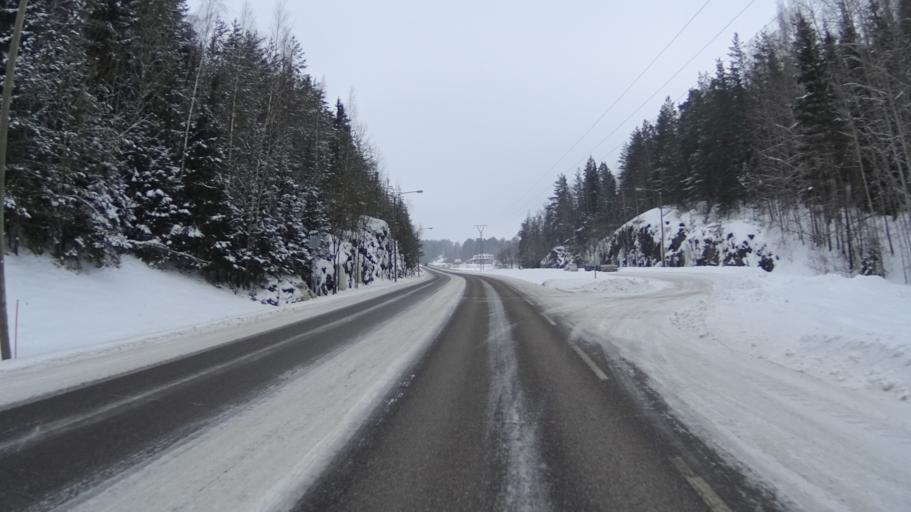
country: FI
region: Uusimaa
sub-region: Helsinki
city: Vihti
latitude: 60.3593
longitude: 24.1750
